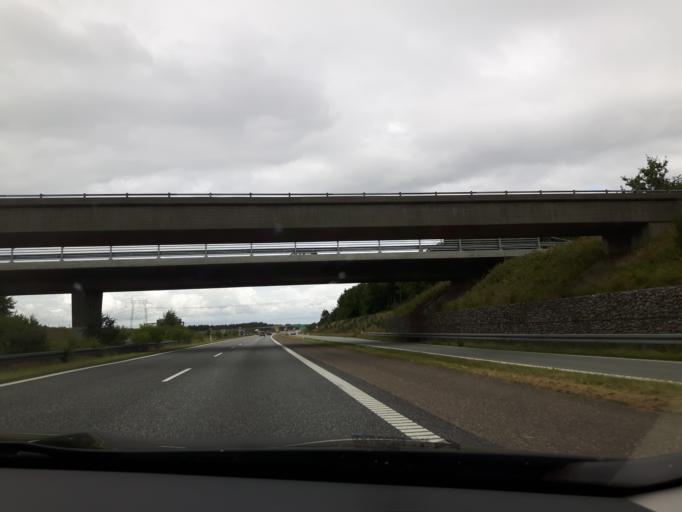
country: DK
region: South Denmark
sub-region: Aabenraa Kommune
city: Krusa
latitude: 54.9388
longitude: 9.3836
